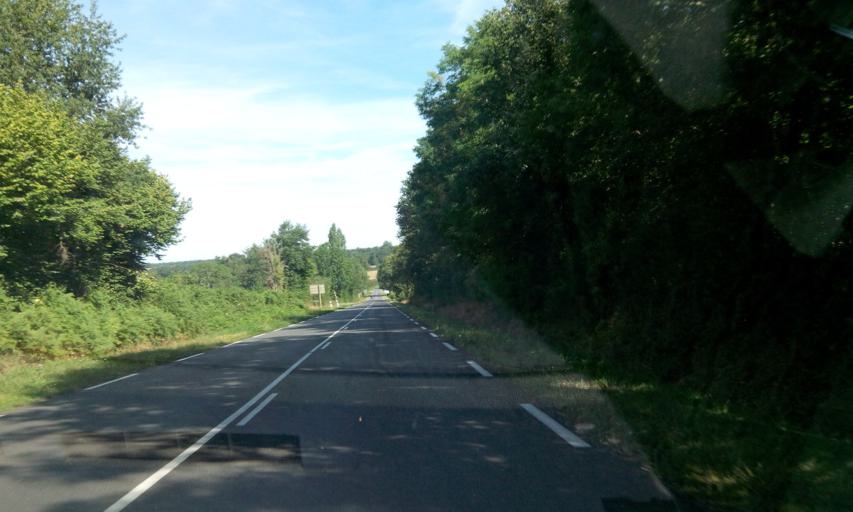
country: FR
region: Poitou-Charentes
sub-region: Departement de la Charente
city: Etagnac
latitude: 45.9226
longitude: 0.7427
